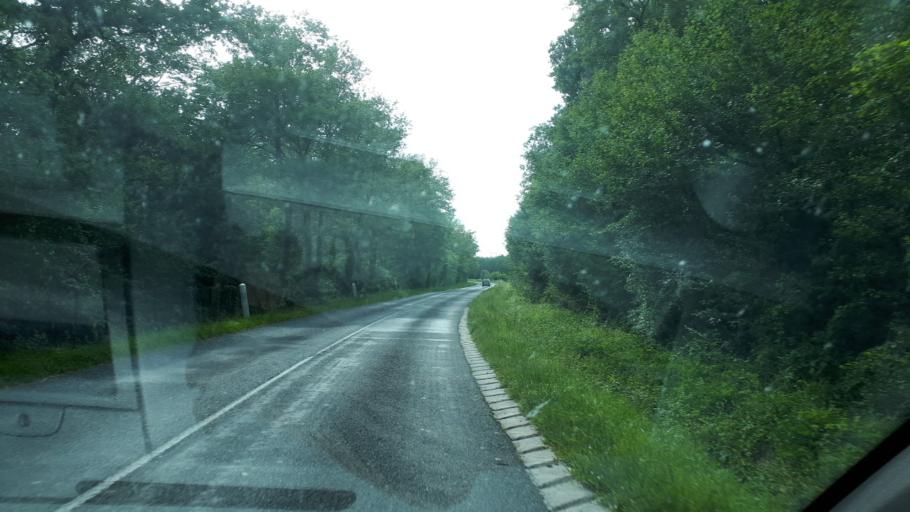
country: FR
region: Centre
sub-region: Departement du Cher
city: Marmagne
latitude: 47.0787
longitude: 2.2923
